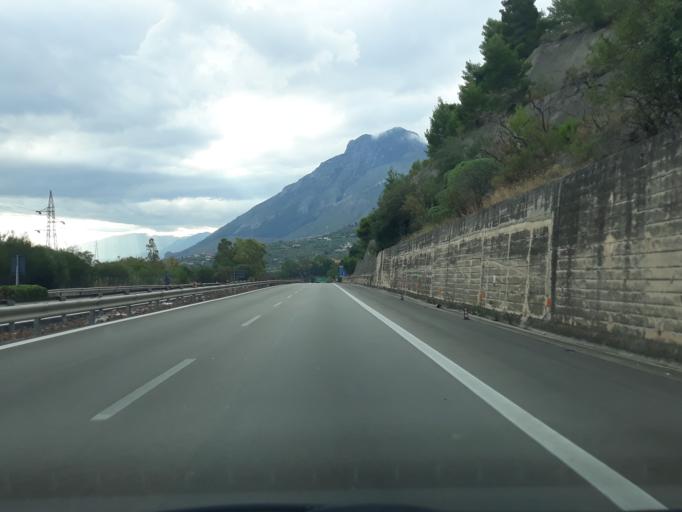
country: IT
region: Sicily
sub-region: Palermo
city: Termini Imerese
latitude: 37.9784
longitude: 13.6747
